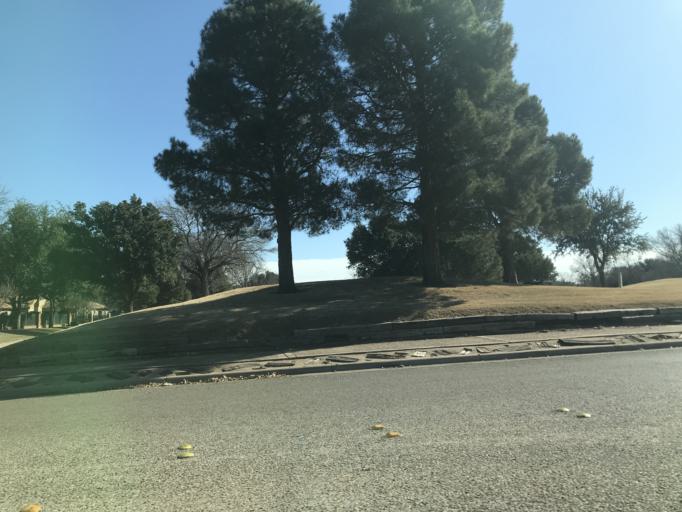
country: US
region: Texas
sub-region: Taylor County
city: Abilene
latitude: 32.3760
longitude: -99.7598
